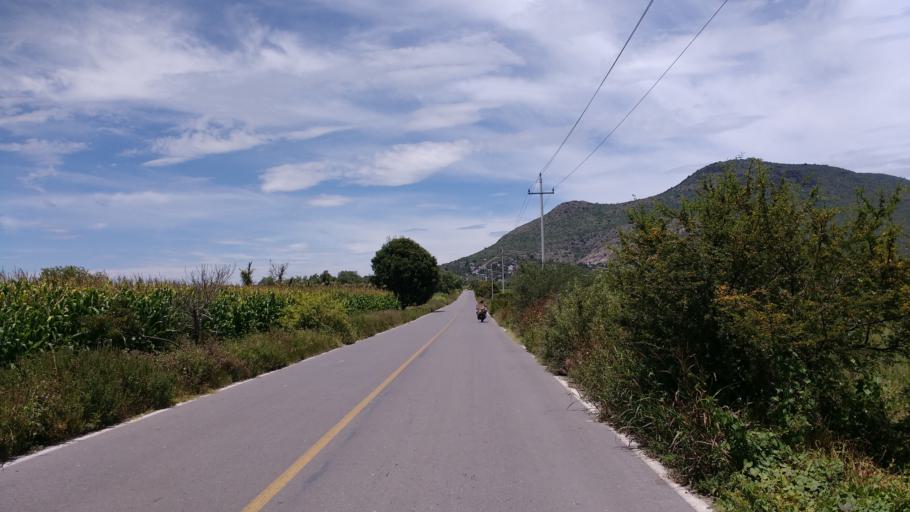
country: MX
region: Hidalgo
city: Mixquiahuala de Juarez
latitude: 20.2372
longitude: -99.2468
